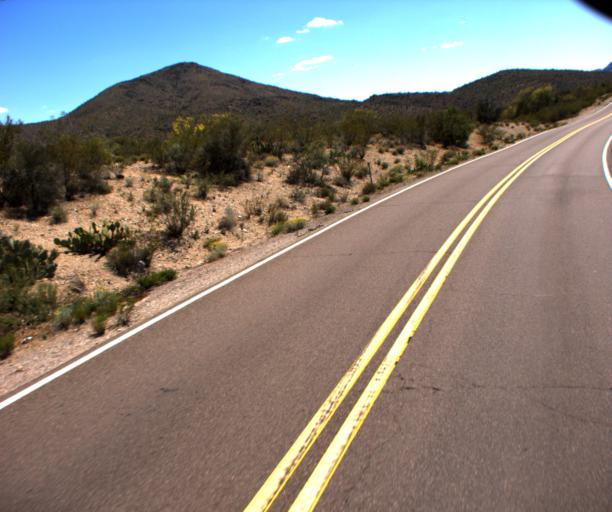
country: US
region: Arizona
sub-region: Yavapai County
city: Bagdad
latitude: 34.4748
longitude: -113.2095
